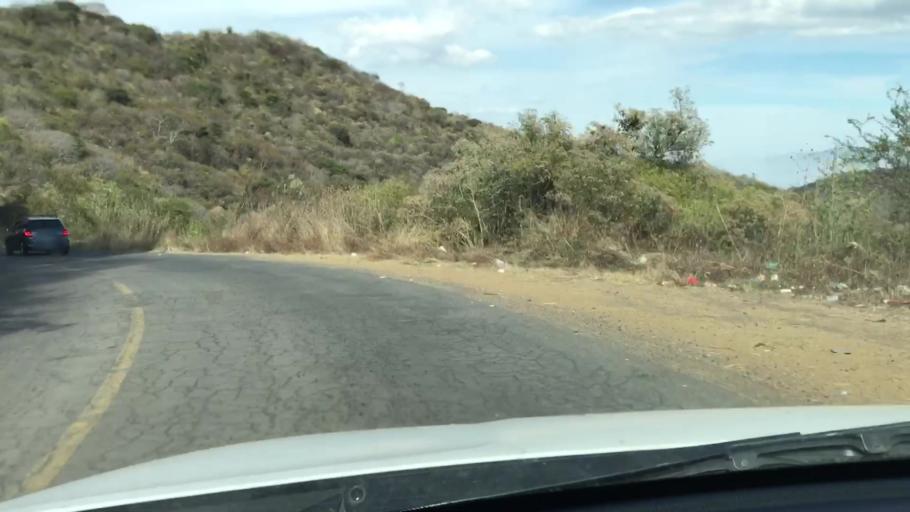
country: MX
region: Jalisco
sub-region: Zacoalco de Torres
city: Barranca de Otates (Barranca de Otatan)
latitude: 20.2412
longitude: -103.6836
